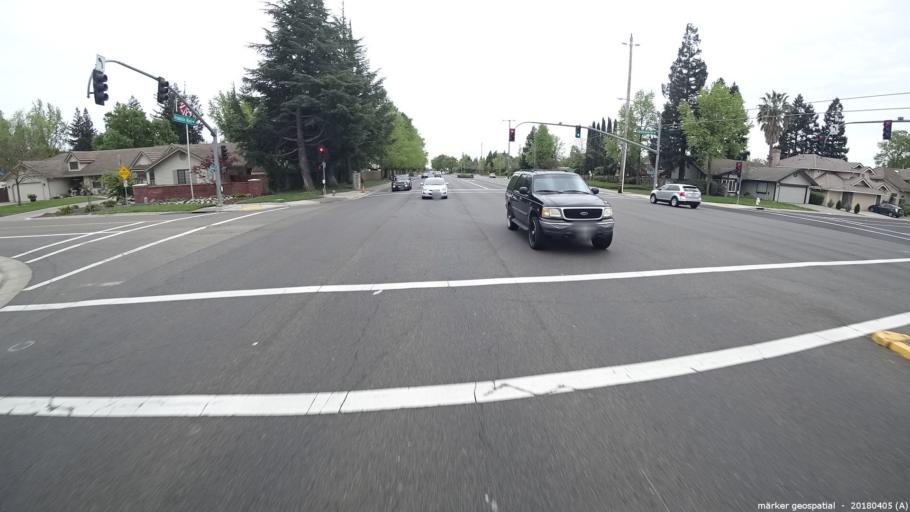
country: US
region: California
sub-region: Sacramento County
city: Laguna
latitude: 38.4140
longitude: -121.4492
